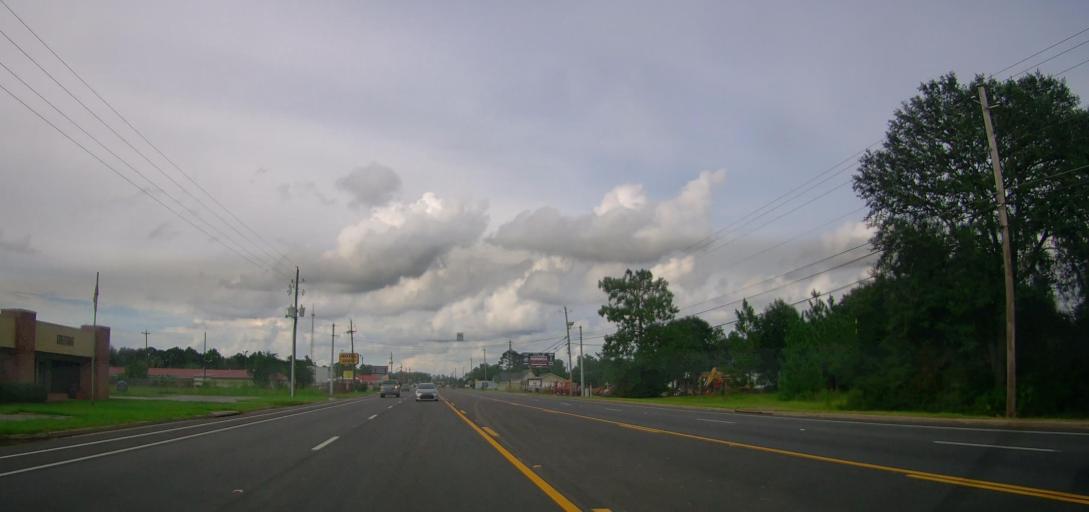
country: US
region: Georgia
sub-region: Wayne County
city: Jesup
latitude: 31.6529
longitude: -81.8530
